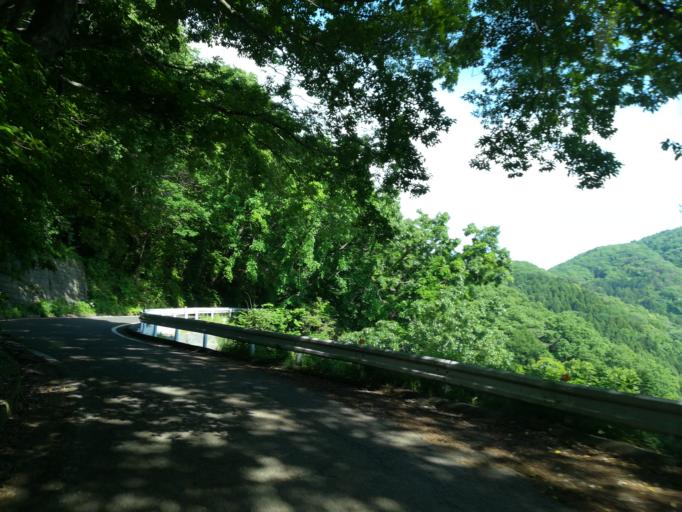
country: JP
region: Ibaraki
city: Tsukuba
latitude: 36.1828
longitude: 140.1308
